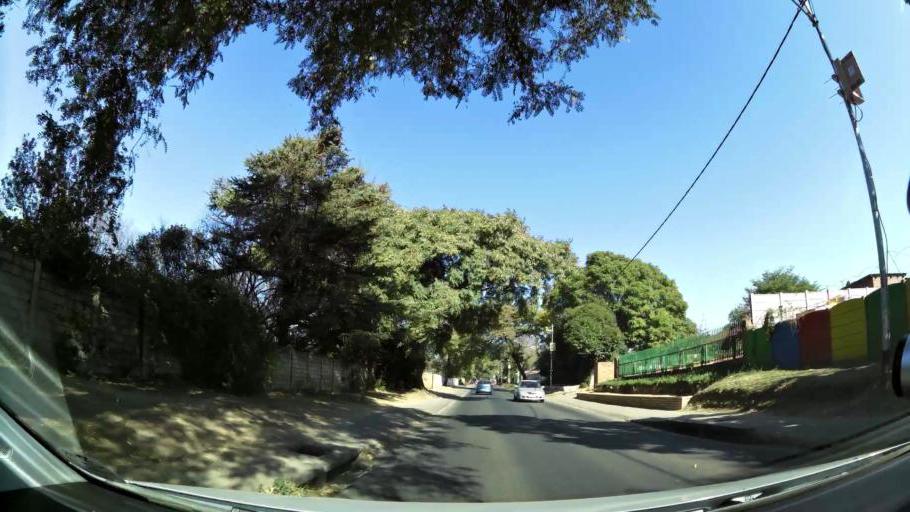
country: ZA
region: Gauteng
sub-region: City of Johannesburg Metropolitan Municipality
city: Modderfontein
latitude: -26.1197
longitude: 28.0950
